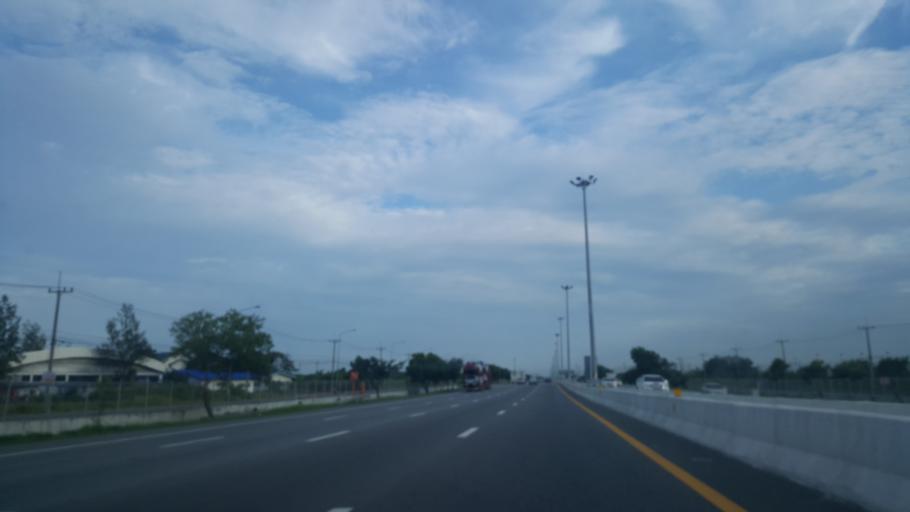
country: TH
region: Chachoengsao
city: Bang Pakong
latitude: 13.5315
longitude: 101.0155
